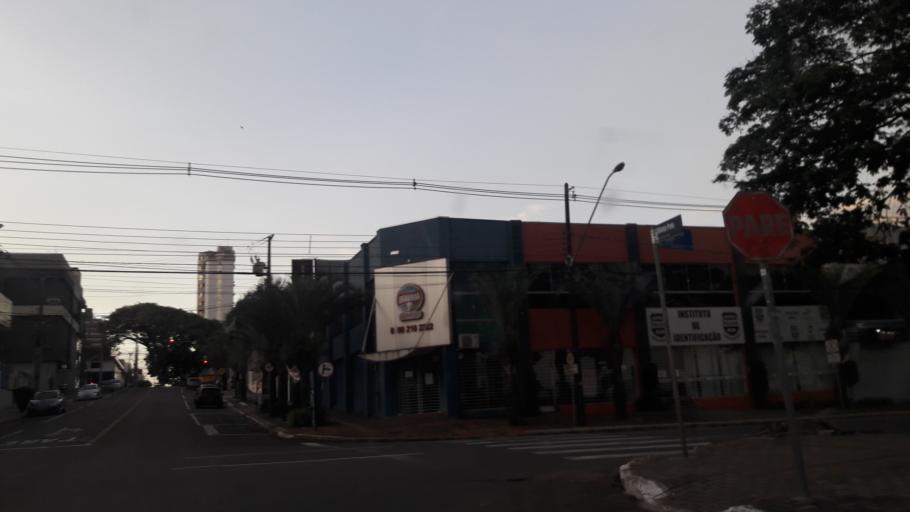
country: BR
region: Parana
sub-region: Cascavel
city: Cascavel
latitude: -24.9549
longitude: -53.4506
